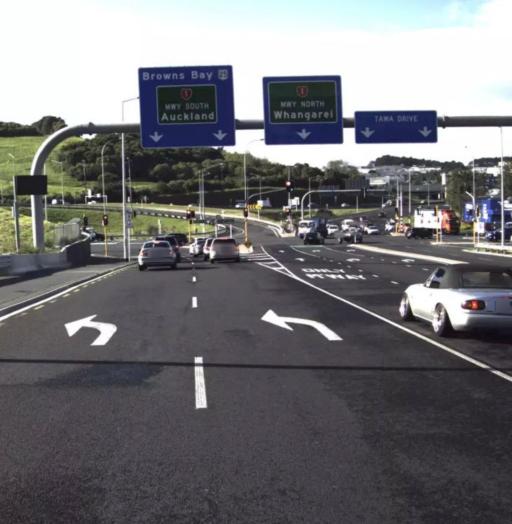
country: NZ
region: Auckland
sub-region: Auckland
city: Rothesay Bay
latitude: -36.7352
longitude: 174.7157
